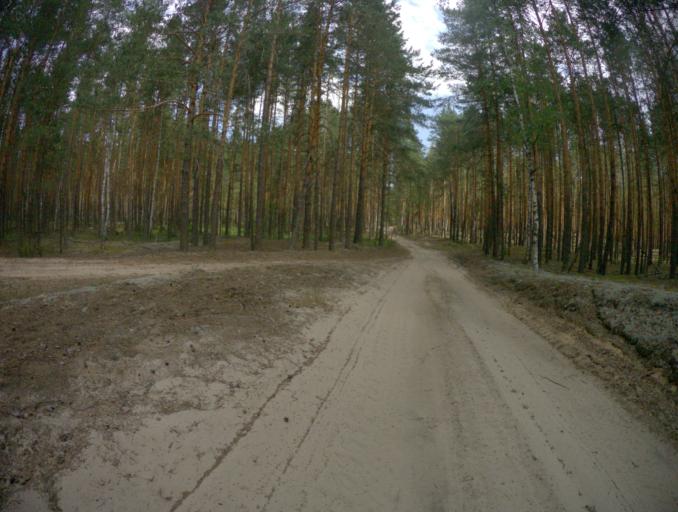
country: RU
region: Ivanovo
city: Talitsy
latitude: 56.3882
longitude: 42.3450
